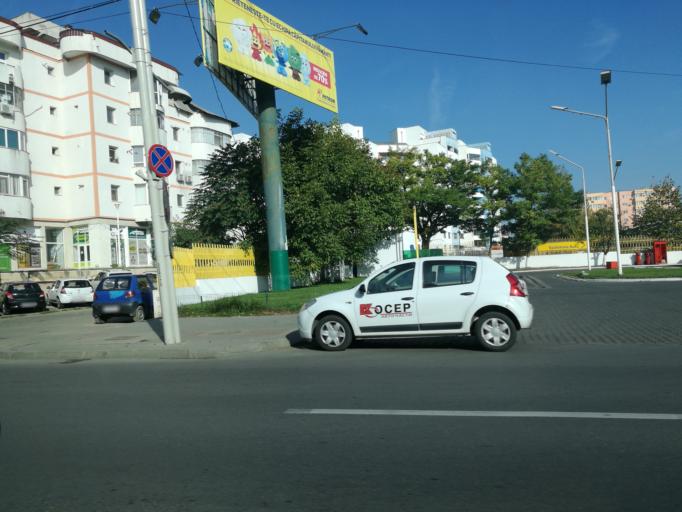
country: RO
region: Iasi
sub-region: Comuna Miroslava
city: Miroslava
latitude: 47.1732
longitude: 27.5345
